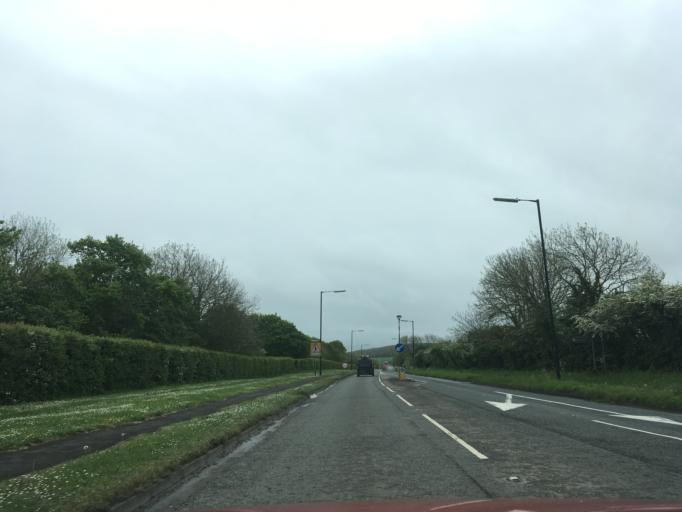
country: GB
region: England
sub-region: North Somerset
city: Hutton
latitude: 51.3344
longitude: -2.9058
